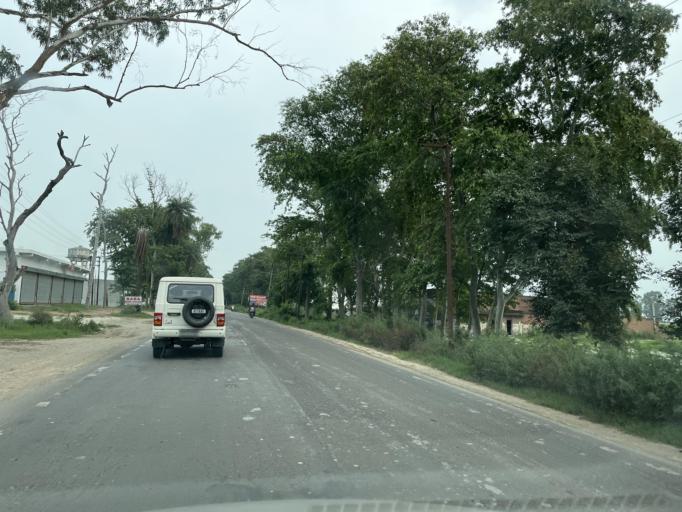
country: IN
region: Uttar Pradesh
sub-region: Rampur
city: Bilaspur
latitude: 29.0288
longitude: 79.2657
